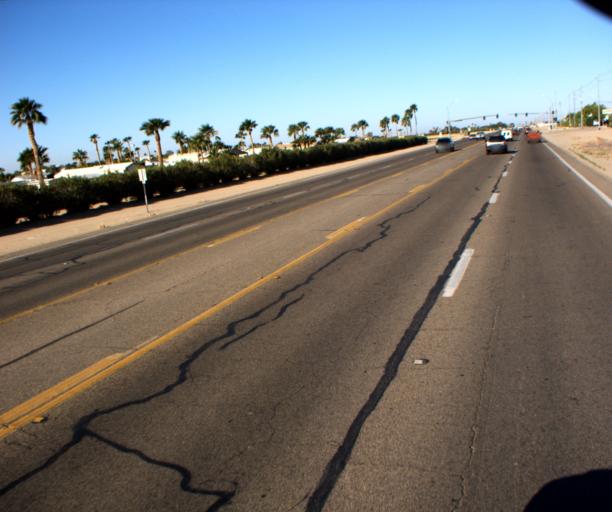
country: US
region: Arizona
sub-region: Yuma County
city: Yuma
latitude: 32.6701
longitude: -114.5362
